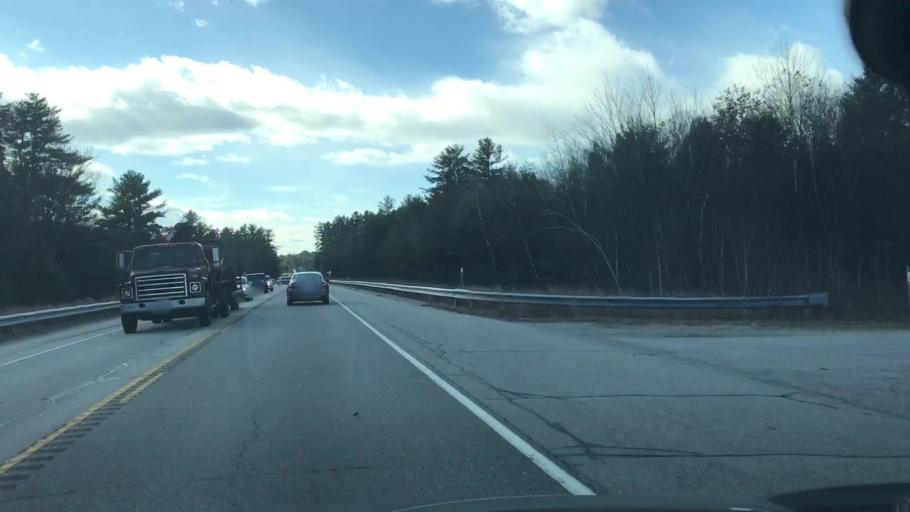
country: US
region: New Hampshire
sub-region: Merrimack County
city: Pittsfield
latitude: 43.3038
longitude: -71.3416
